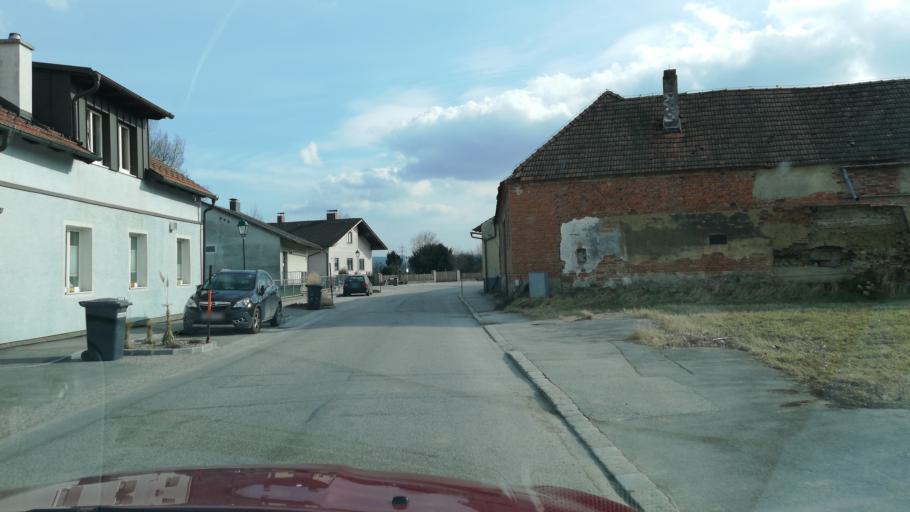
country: AT
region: Lower Austria
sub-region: Politischer Bezirk Tulln
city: Langenrohr
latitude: 48.3172
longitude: 16.0116
